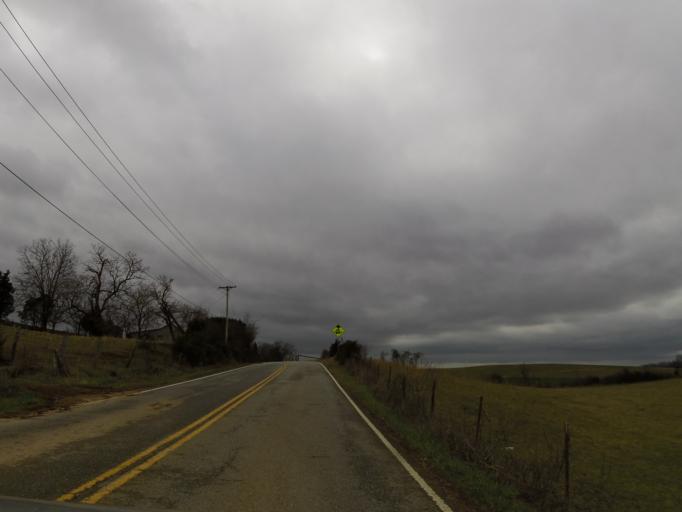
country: US
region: Tennessee
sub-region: Grainger County
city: Rutledge
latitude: 36.1979
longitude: -83.5442
